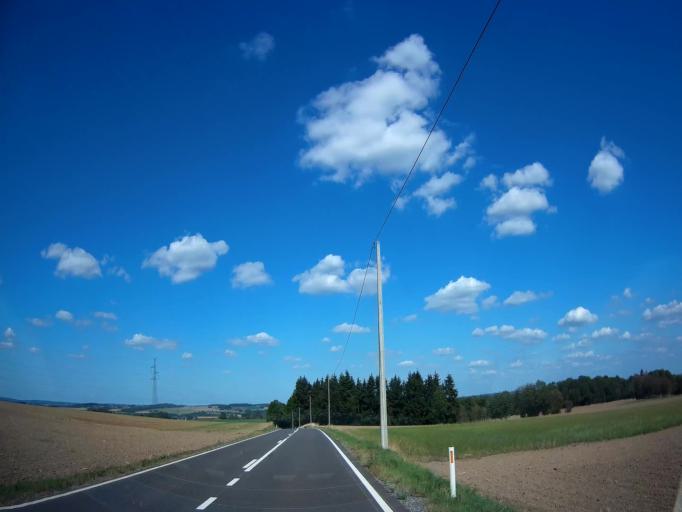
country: BE
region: Wallonia
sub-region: Province de Namur
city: Houyet
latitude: 50.1870
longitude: 4.9346
